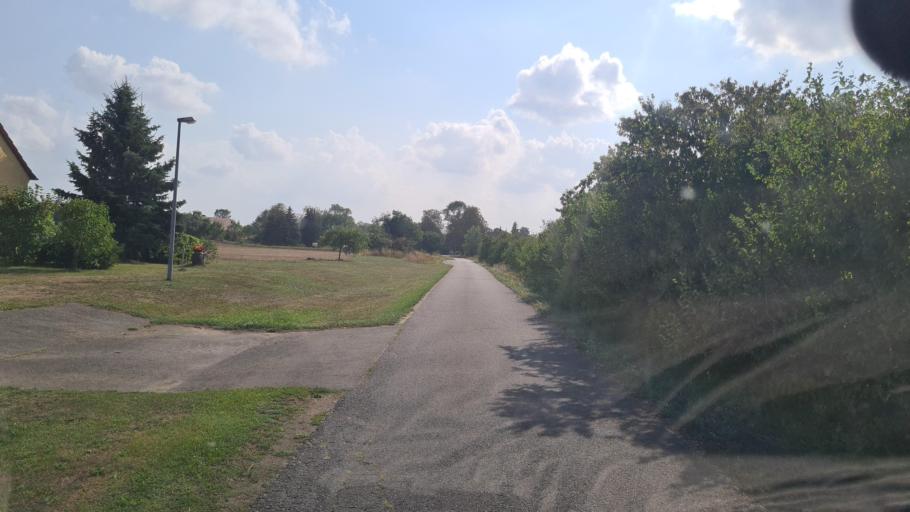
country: DE
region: Brandenburg
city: Dahme
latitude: 51.9027
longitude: 13.4128
